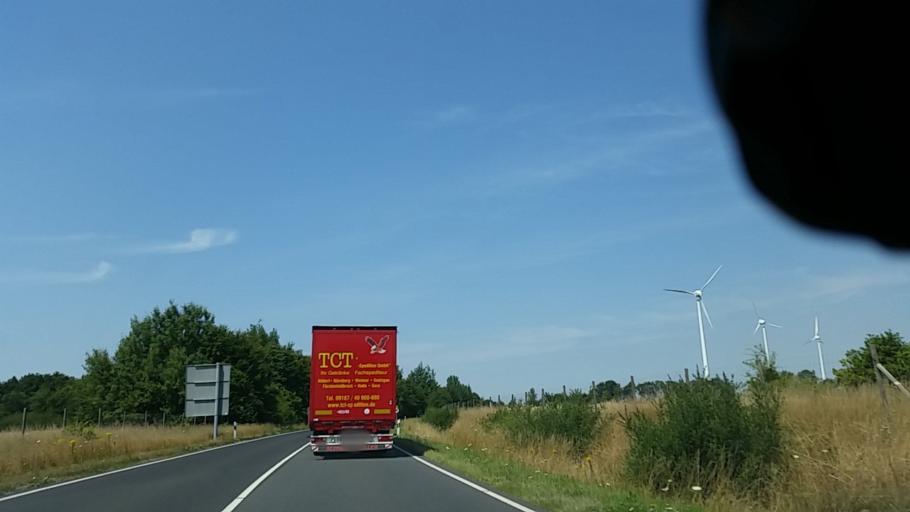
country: DE
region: Lower Saxony
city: Binnen
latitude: 52.6596
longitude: 9.1053
